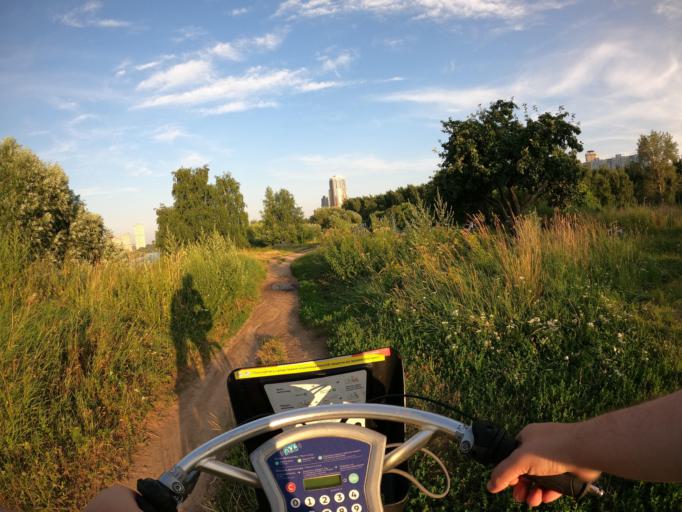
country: RU
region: Moscow
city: Strogino
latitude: 55.8117
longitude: 37.4169
